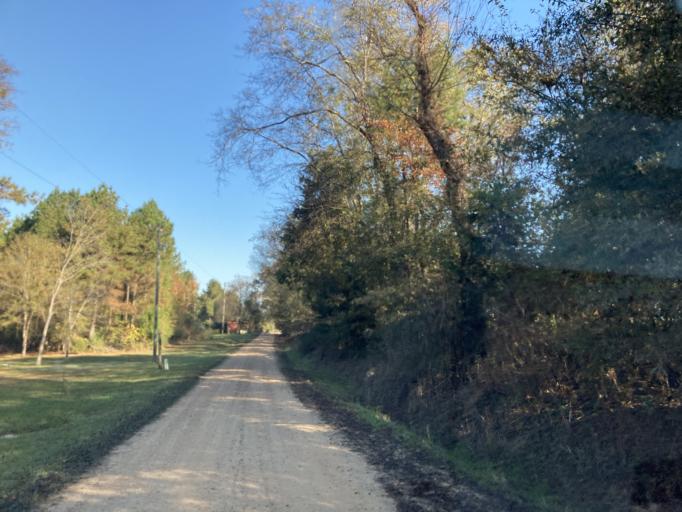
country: US
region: Mississippi
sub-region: Madison County
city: Canton
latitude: 32.7275
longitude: -90.1752
